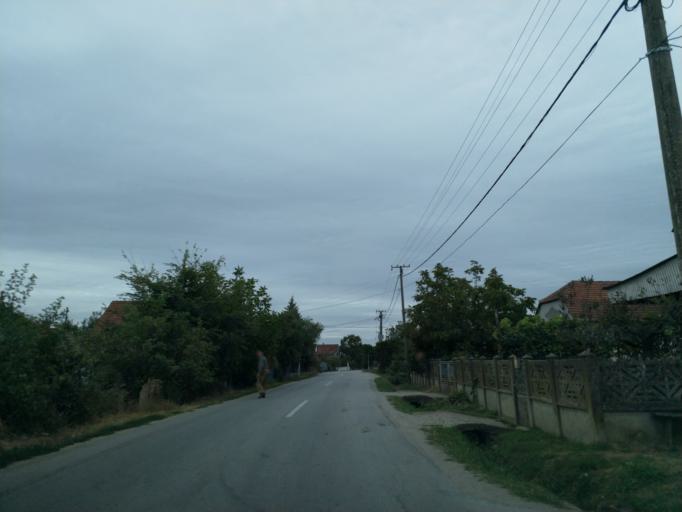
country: RS
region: Central Serbia
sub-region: Pomoravski Okrug
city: Cuprija
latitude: 43.8651
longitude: 21.3232
